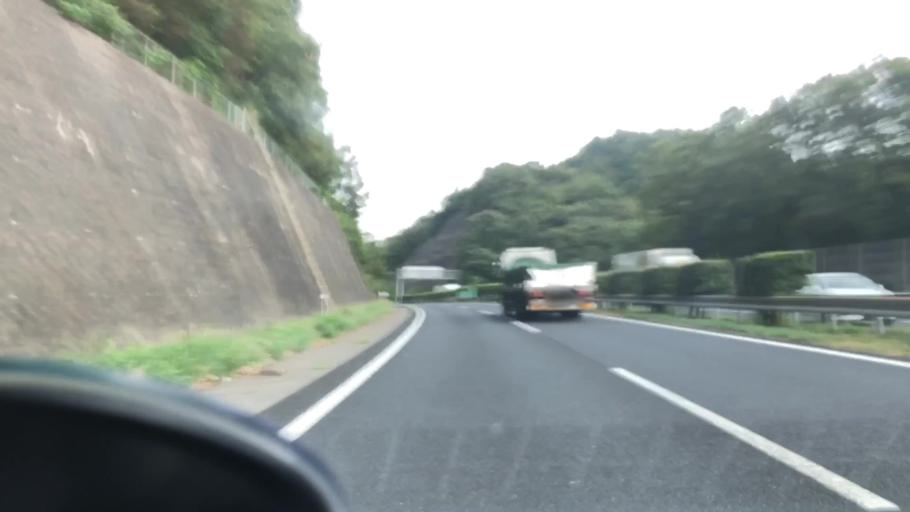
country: JP
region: Hyogo
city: Ono
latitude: 34.9334
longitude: 134.8455
